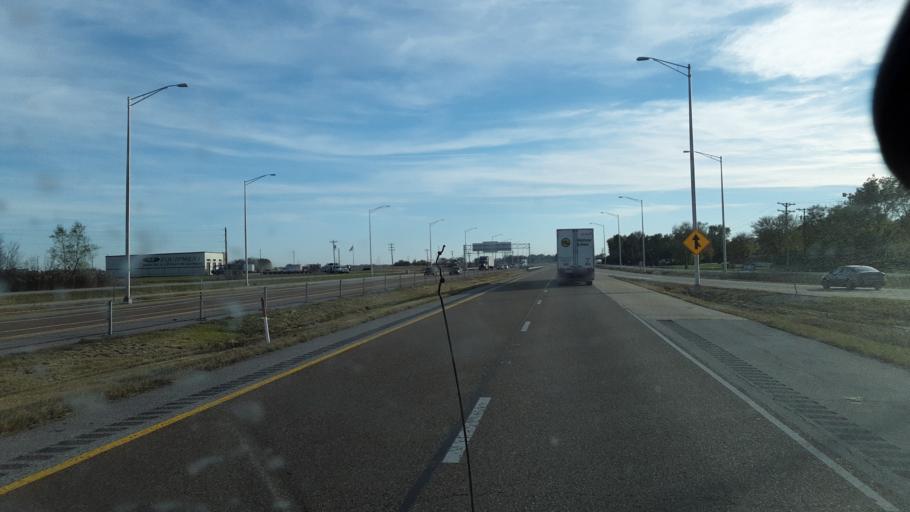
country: US
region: Illinois
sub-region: Madison County
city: Troy
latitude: 38.7305
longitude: -89.9132
